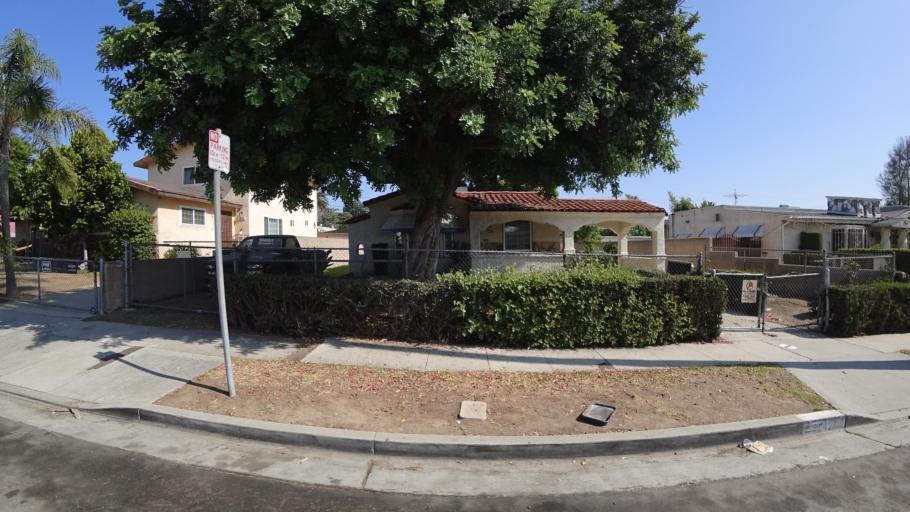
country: US
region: California
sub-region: Los Angeles County
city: Westmont
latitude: 33.9432
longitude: -118.3013
